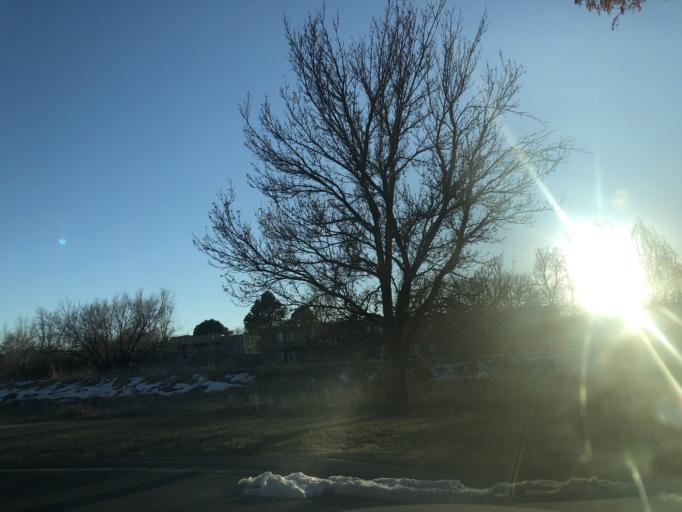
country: US
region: Colorado
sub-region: Adams County
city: Aurora
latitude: 39.7181
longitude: -104.8179
